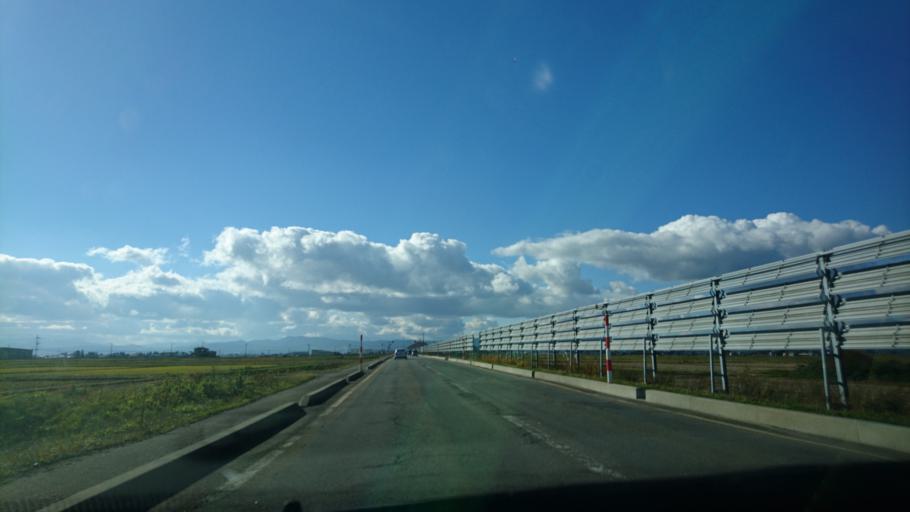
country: JP
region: Akita
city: Yokotemachi
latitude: 39.2675
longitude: 140.4808
